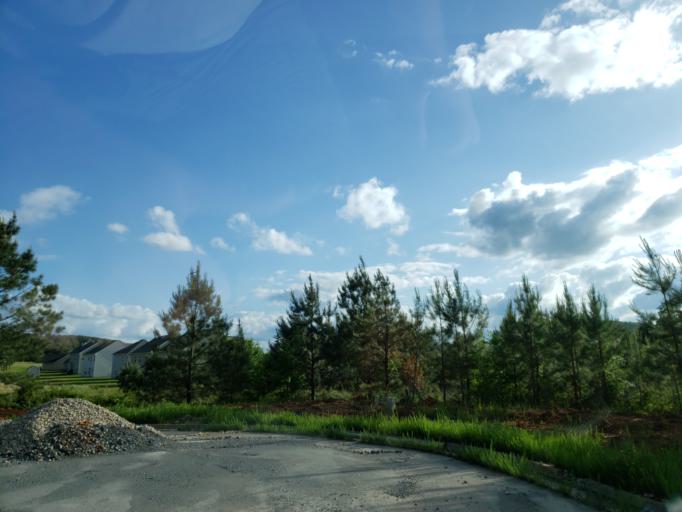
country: US
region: Georgia
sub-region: Bartow County
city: Adairsville
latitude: 34.3909
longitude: -84.8946
